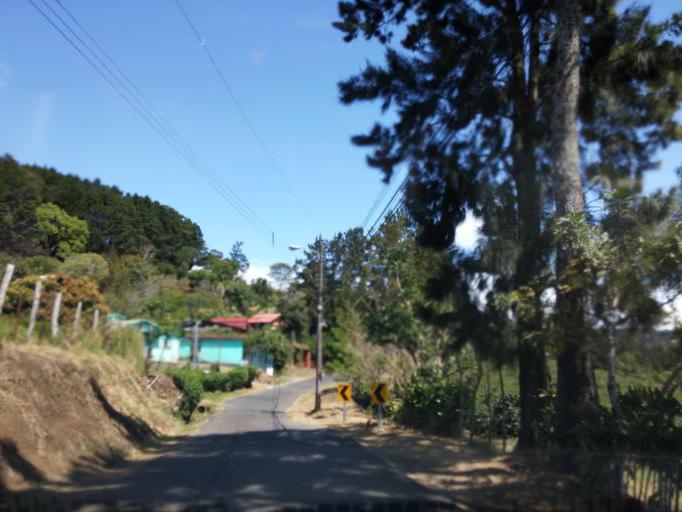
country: CR
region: Heredia
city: Santo Domingo
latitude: 10.0637
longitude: -84.1308
